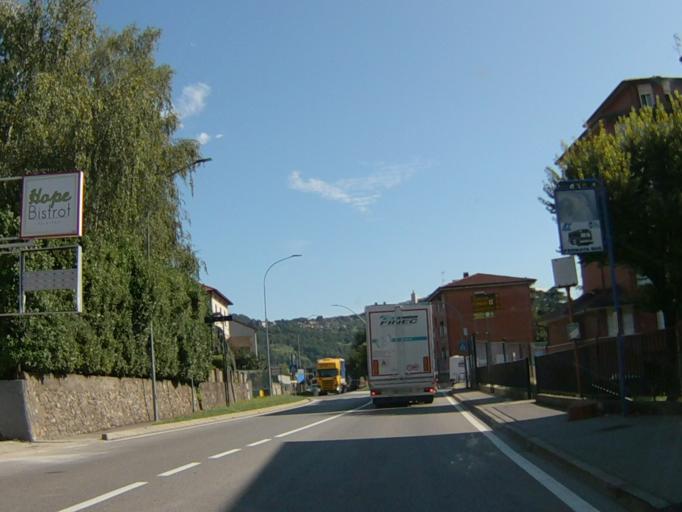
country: IT
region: Lombardy
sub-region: Provincia di Lecco
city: Calolziocorte
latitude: 45.7939
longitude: 9.4370
